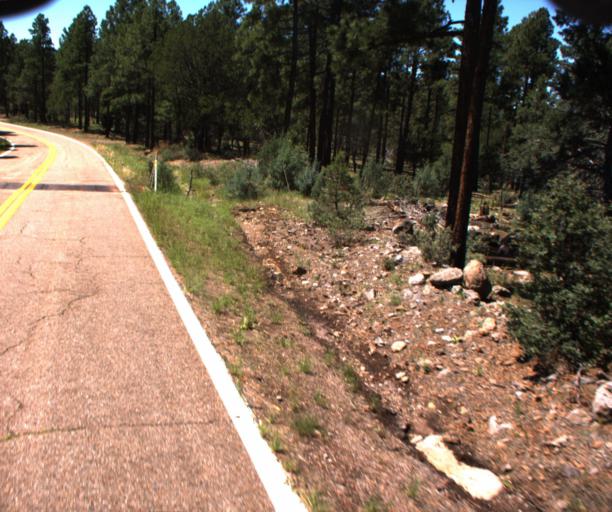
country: US
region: Arizona
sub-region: Greenlee County
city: Morenci
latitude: 33.5107
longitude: -109.3227
